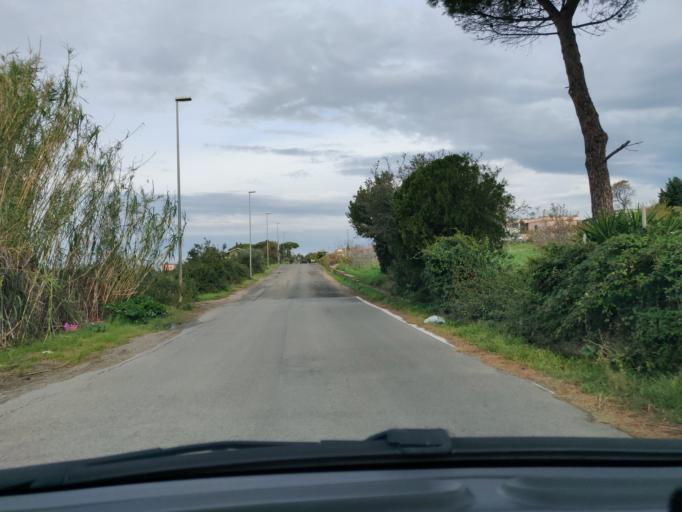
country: IT
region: Latium
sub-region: Citta metropolitana di Roma Capitale
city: Civitavecchia
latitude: 42.1009
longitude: 11.8132
